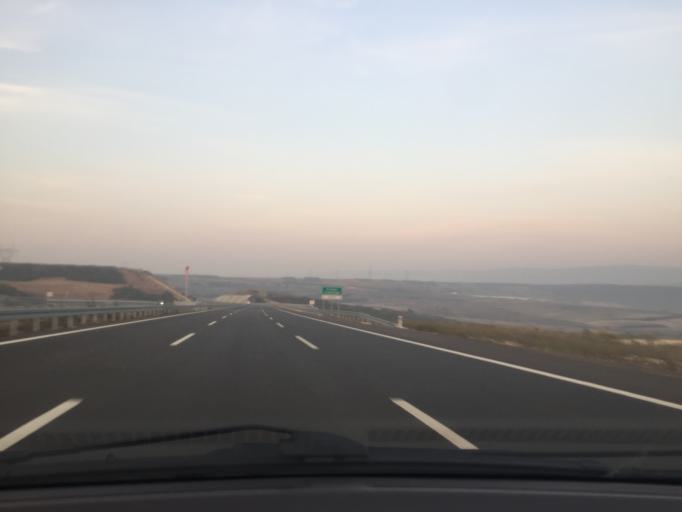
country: TR
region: Bursa
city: Mahmudiye
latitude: 40.2767
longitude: 28.5256
